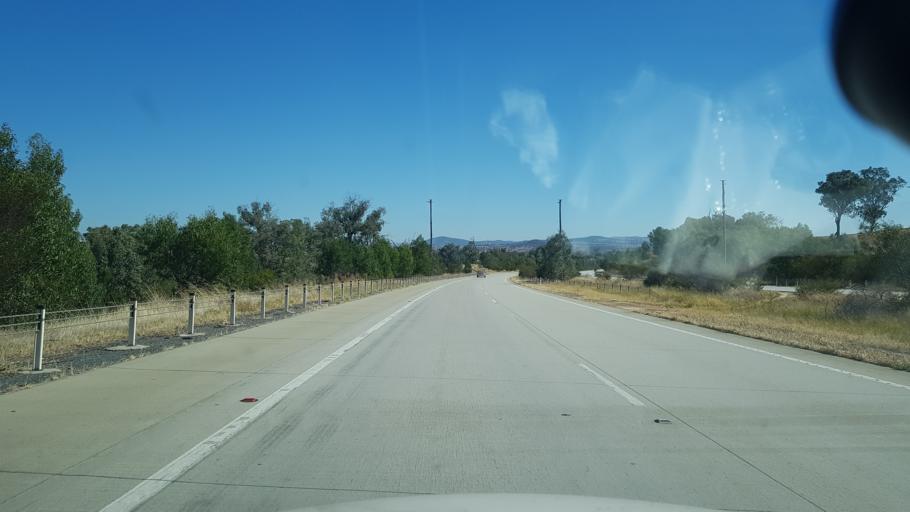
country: AU
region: New South Wales
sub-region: Albury Municipality
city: Lavington
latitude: -35.9238
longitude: 147.0917
